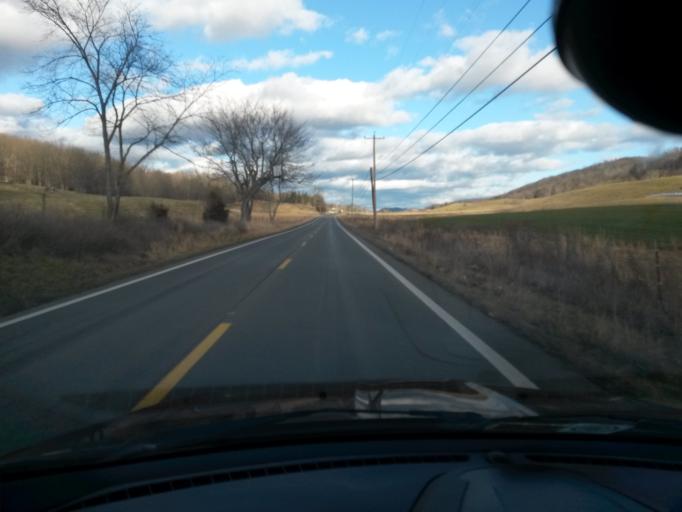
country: US
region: Virginia
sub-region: Giles County
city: Pearisburg
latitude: 37.4216
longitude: -80.7356
